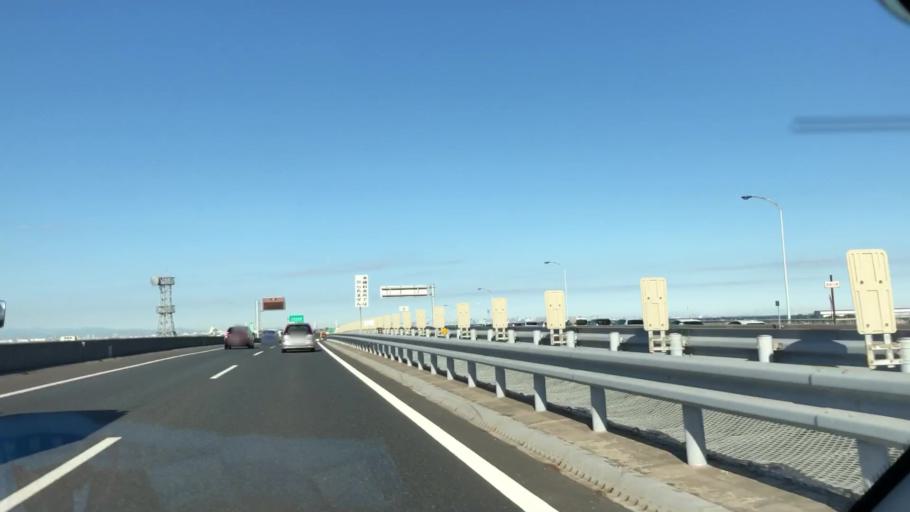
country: JP
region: Chiba
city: Kisarazu
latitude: 35.4246
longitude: 139.9323
